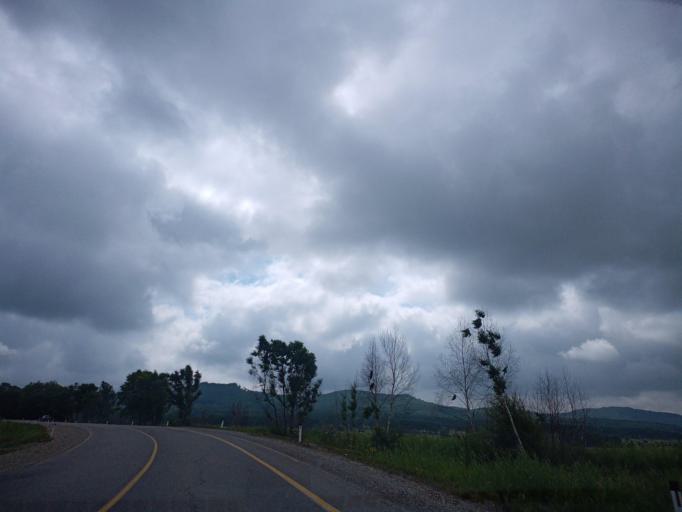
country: RU
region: Primorskiy
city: Dal'nerechensk
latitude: 46.0379
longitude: 133.8857
